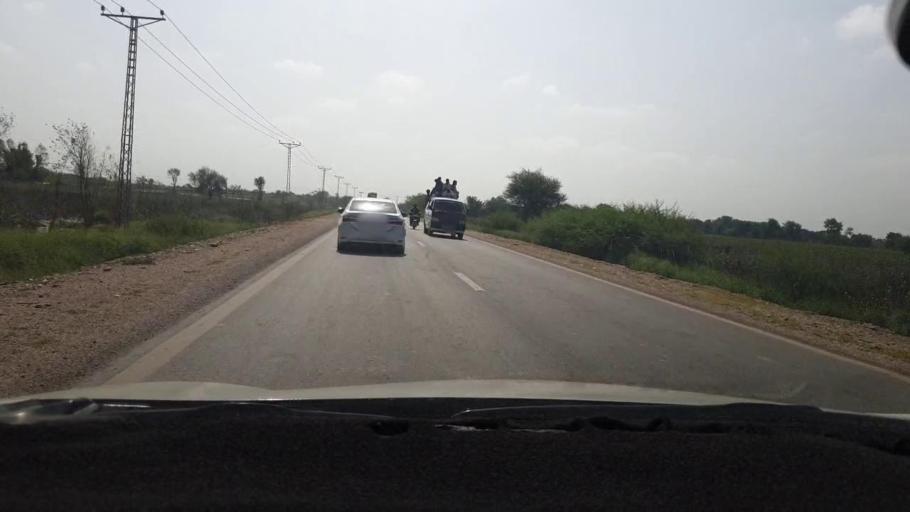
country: PK
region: Sindh
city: Mirpur Khas
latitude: 25.7598
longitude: 69.0809
